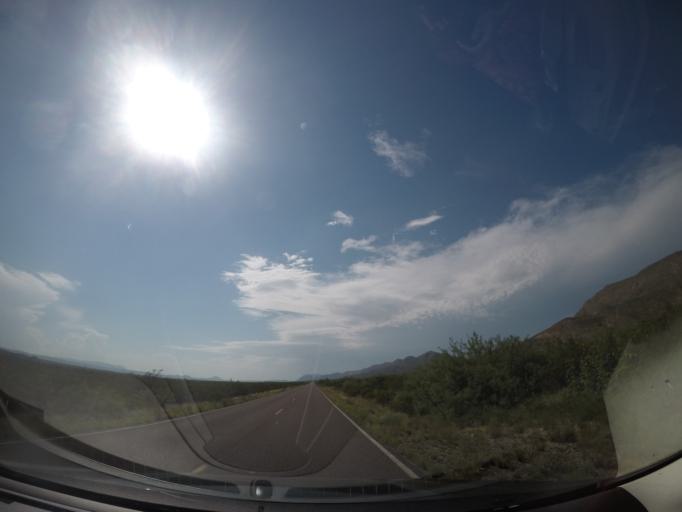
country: US
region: Texas
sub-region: Brewster County
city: Alpine
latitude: 29.6417
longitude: -103.1652
